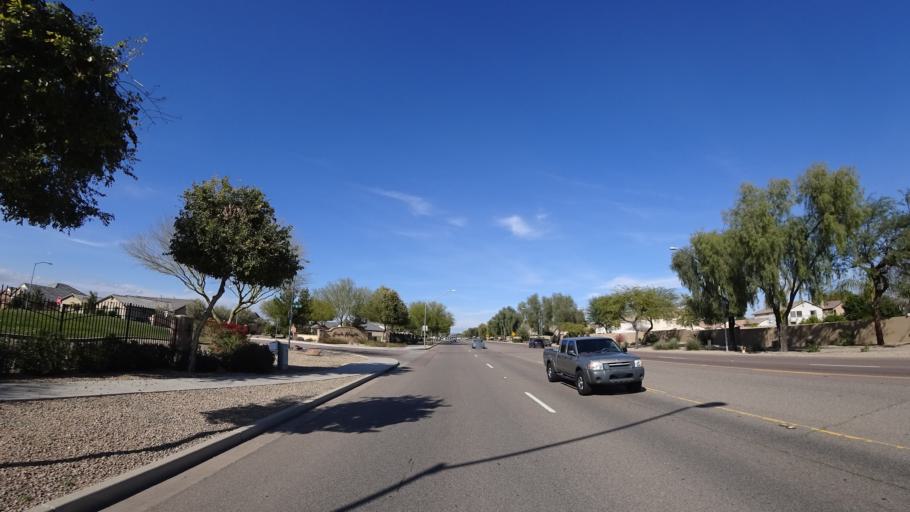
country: US
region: Arizona
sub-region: Maricopa County
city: Sun City
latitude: 33.6766
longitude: -112.2205
